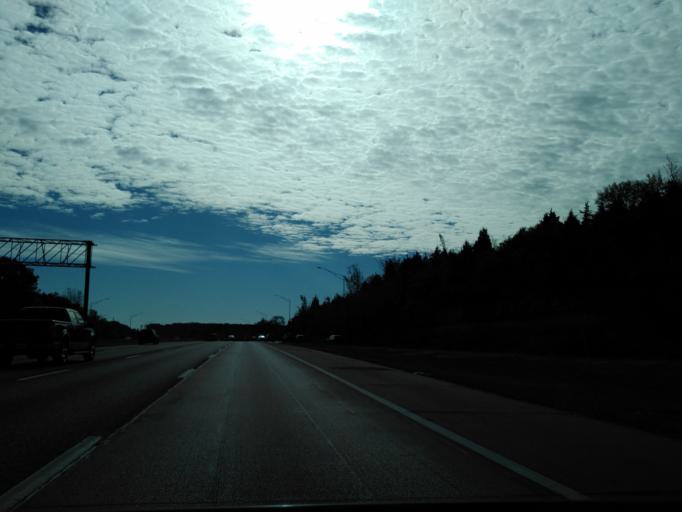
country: US
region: Missouri
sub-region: Saint Louis County
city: Sunset Hills
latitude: 38.5496
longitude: -90.4281
